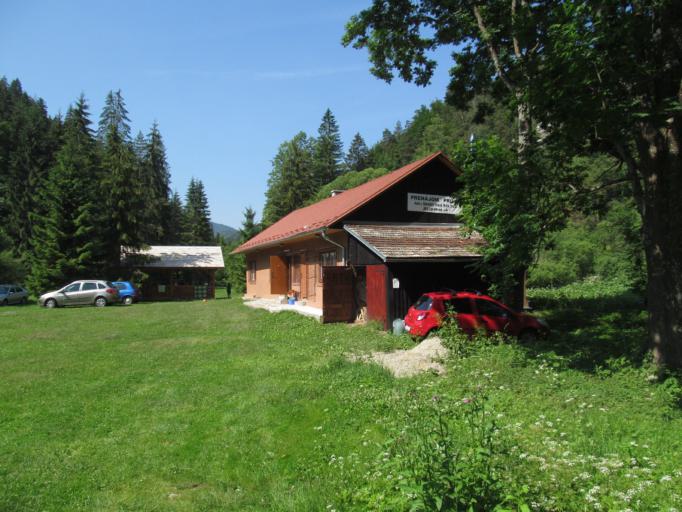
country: SK
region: Kosicky
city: Dobsina
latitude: 48.9329
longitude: 20.3340
